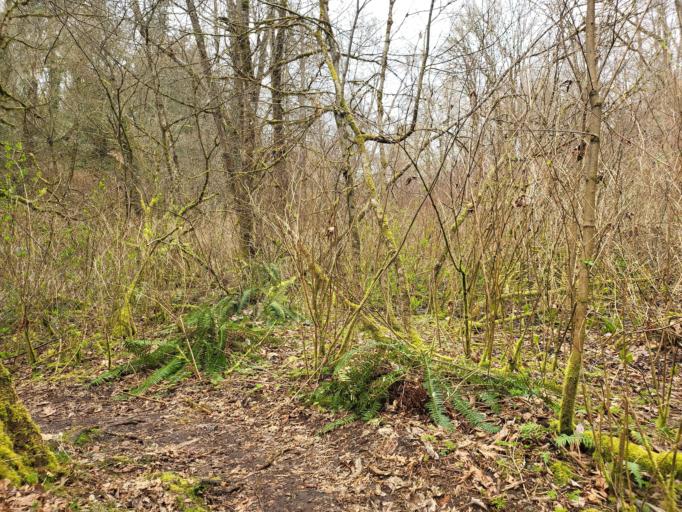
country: US
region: Washington
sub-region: King County
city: Kent
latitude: 47.3795
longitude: -122.2185
